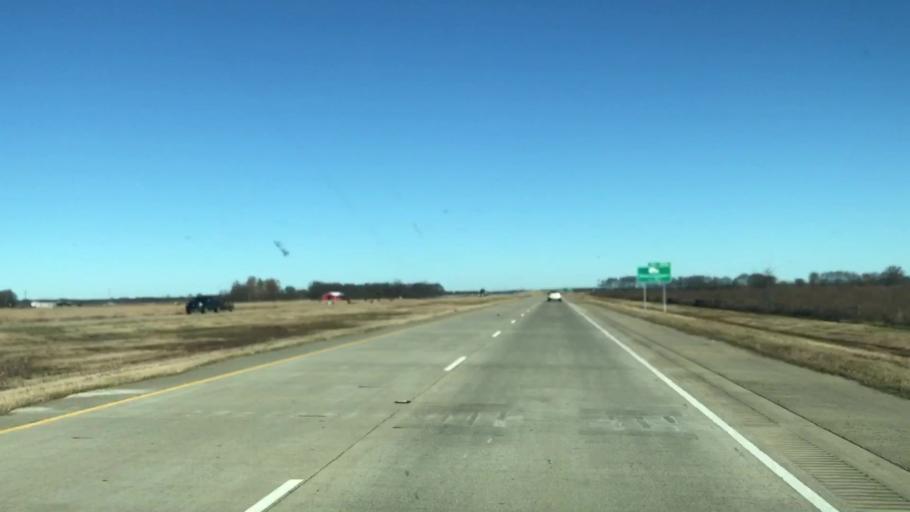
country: US
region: Louisiana
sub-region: Bossier Parish
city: Benton
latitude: 32.6894
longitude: -93.8560
